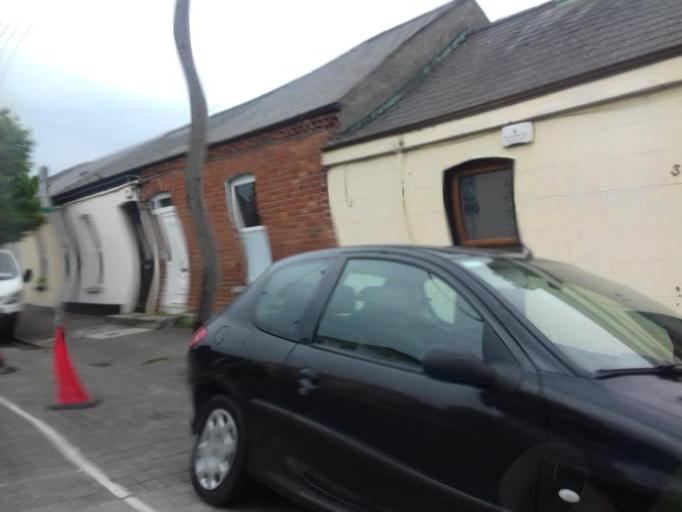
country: IE
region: Leinster
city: Drumcondra
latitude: 53.3612
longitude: -6.2637
